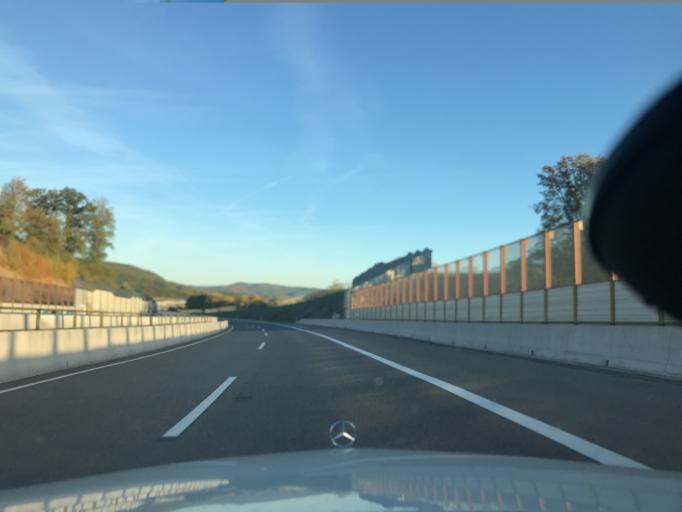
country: DE
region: Hesse
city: Waldkappel
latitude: 51.1525
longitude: 9.8962
